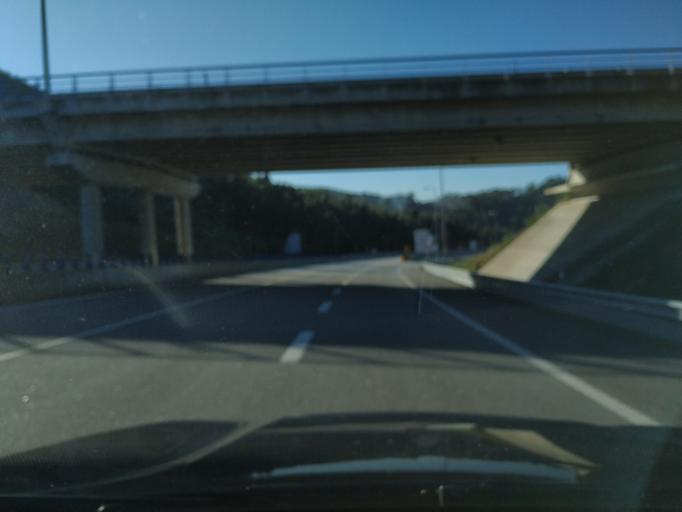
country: PT
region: Aveiro
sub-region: Oliveira de Azemeis
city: Vila Cha
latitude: 40.8749
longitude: -8.4318
